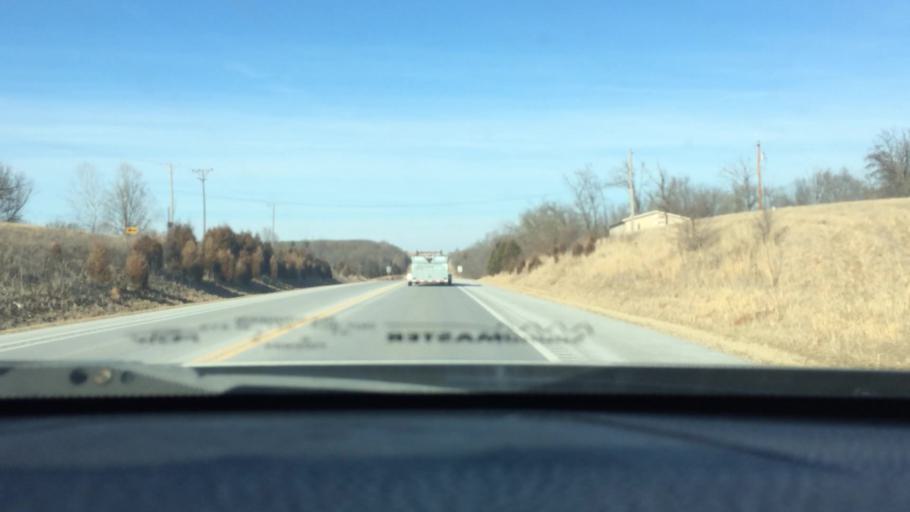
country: US
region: Missouri
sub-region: Newton County
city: Neosho
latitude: 36.8926
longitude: -94.3171
